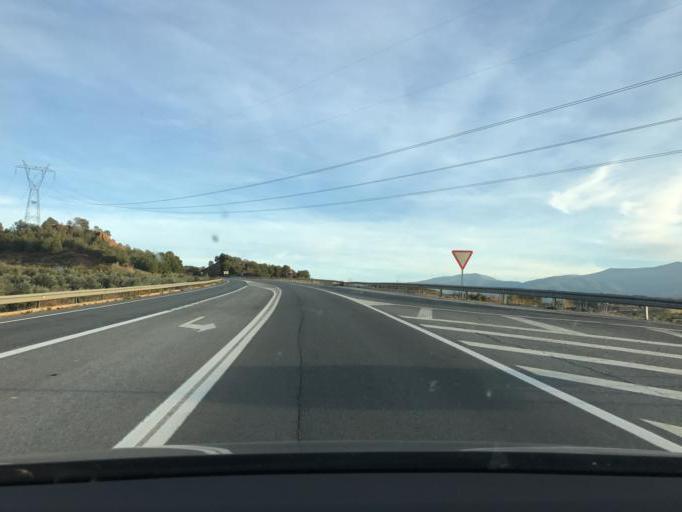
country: ES
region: Andalusia
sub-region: Provincia de Granada
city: Guadix
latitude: 37.2742
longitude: -3.1092
